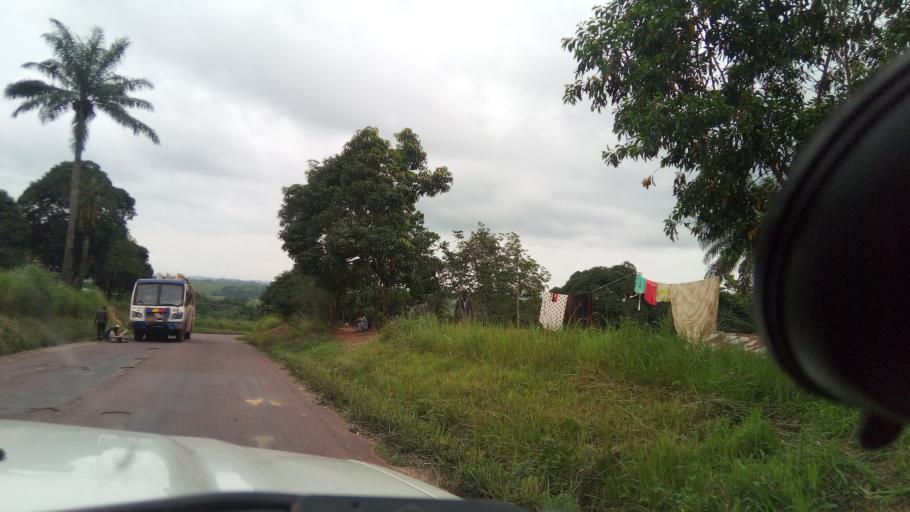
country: CD
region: Bas-Congo
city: Kasangulu
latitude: -4.9072
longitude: 15.1638
